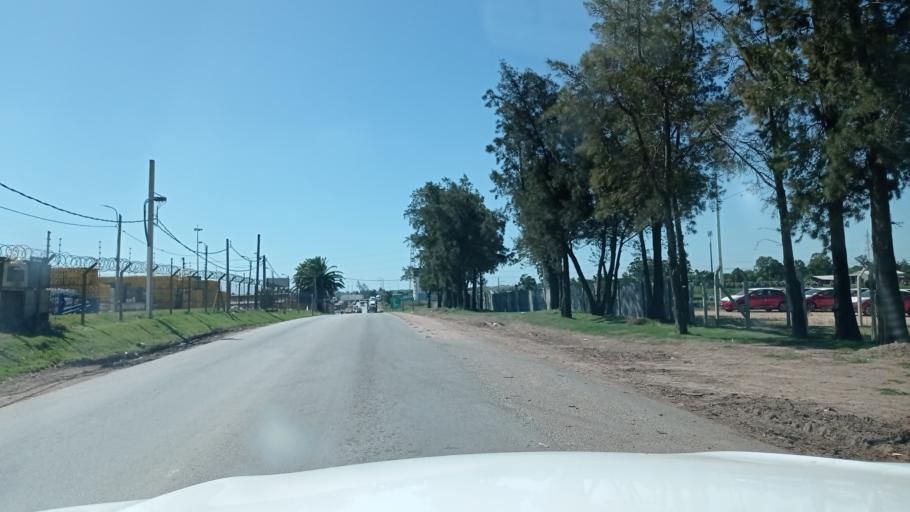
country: UY
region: Montevideo
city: Pajas Blancas
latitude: -34.8551
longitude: -56.2897
